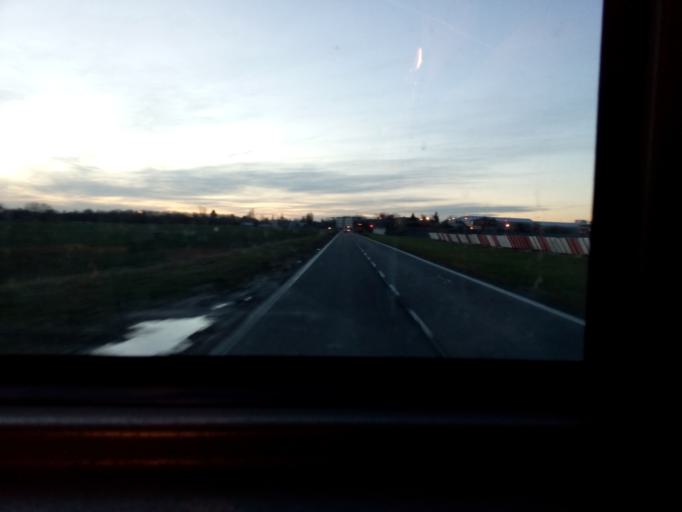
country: CZ
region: Central Bohemia
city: Tuchomerice
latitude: 50.1052
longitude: 14.2874
